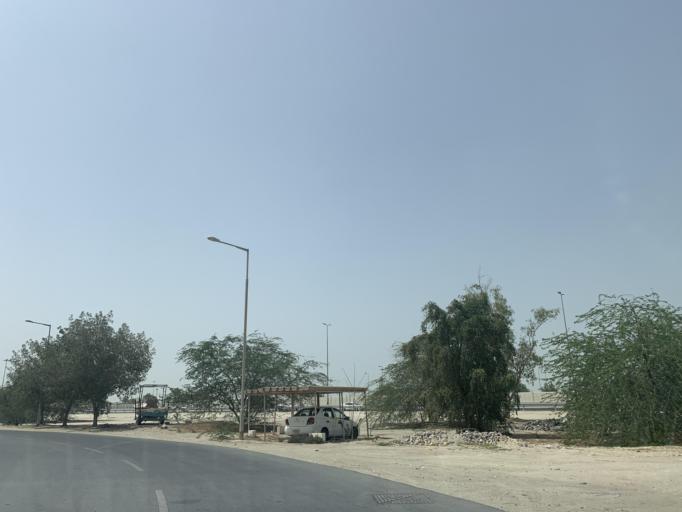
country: BH
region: Northern
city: Madinat `Isa
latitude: 26.1572
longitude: 50.5325
